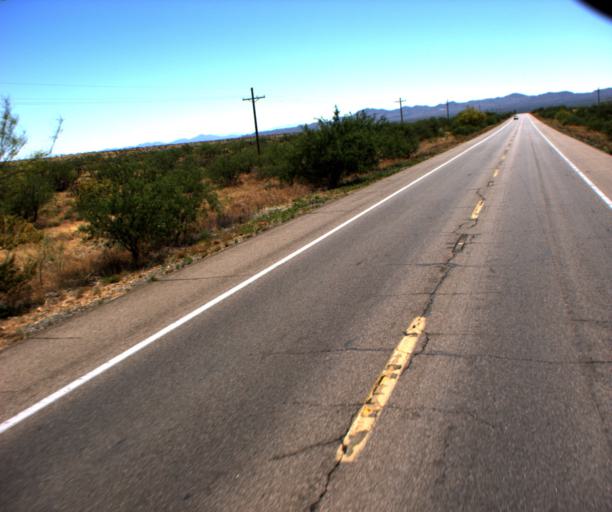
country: US
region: Arizona
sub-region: Pima County
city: Catalina
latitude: 32.5984
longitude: -110.8770
